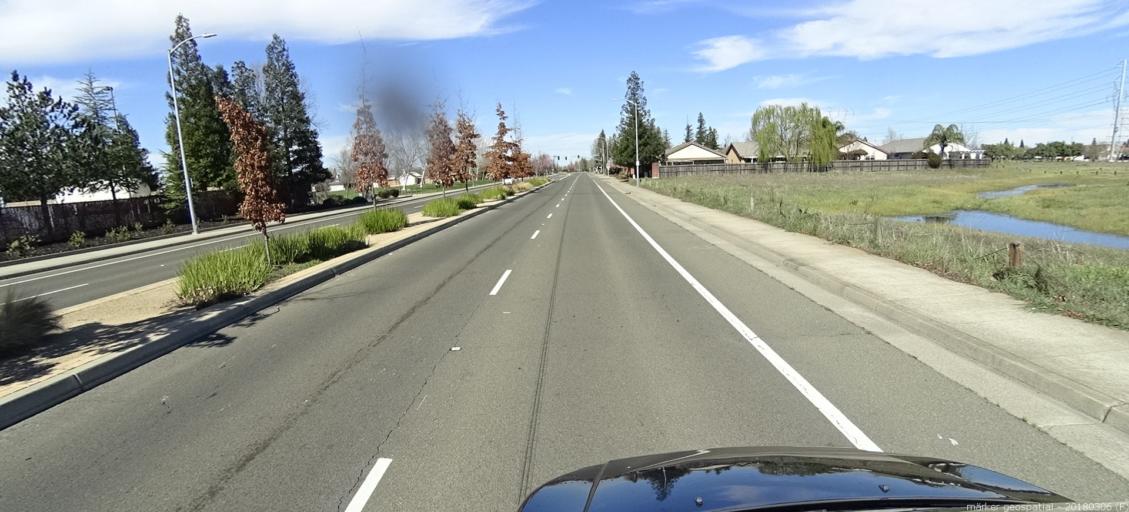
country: US
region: California
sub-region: Sacramento County
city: Vineyard
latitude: 38.4584
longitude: -121.3541
